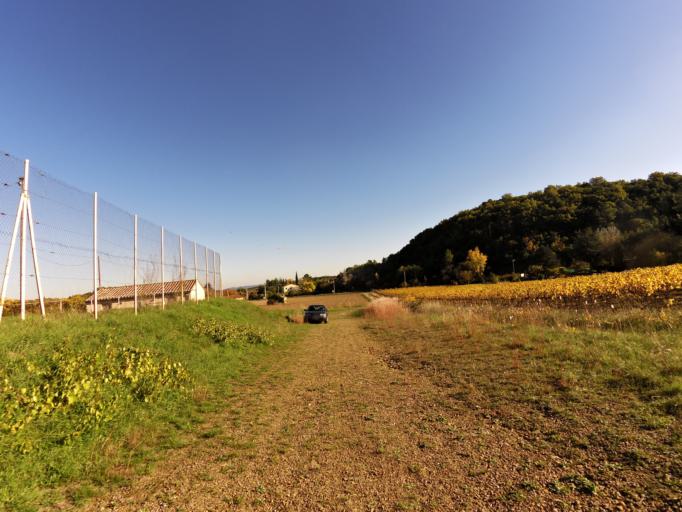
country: FR
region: Languedoc-Roussillon
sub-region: Departement du Gard
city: Sauve
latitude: 43.9902
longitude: 3.9476
